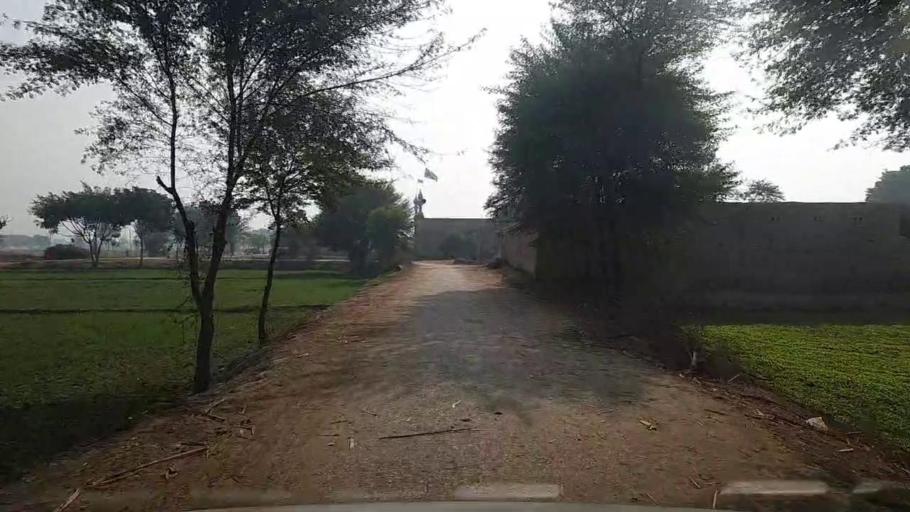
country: PK
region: Sindh
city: Setharja Old
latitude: 27.1246
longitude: 68.5155
